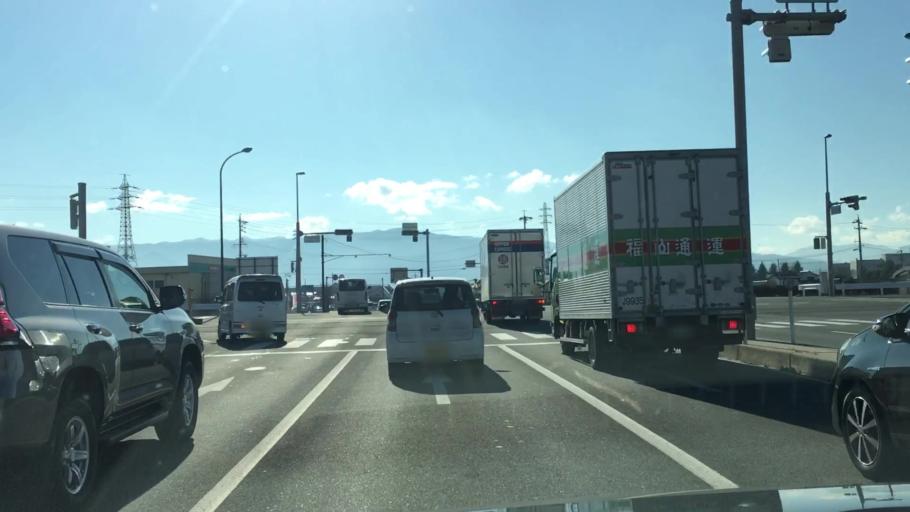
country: JP
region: Nagano
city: Nagano-shi
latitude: 36.6036
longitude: 138.1791
